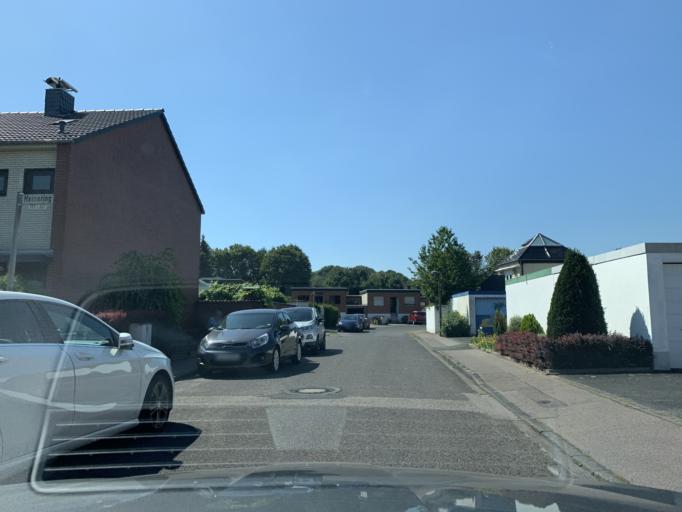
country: DE
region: North Rhine-Westphalia
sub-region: Regierungsbezirk Koln
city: Mengenich
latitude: 50.9929
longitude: 6.8729
